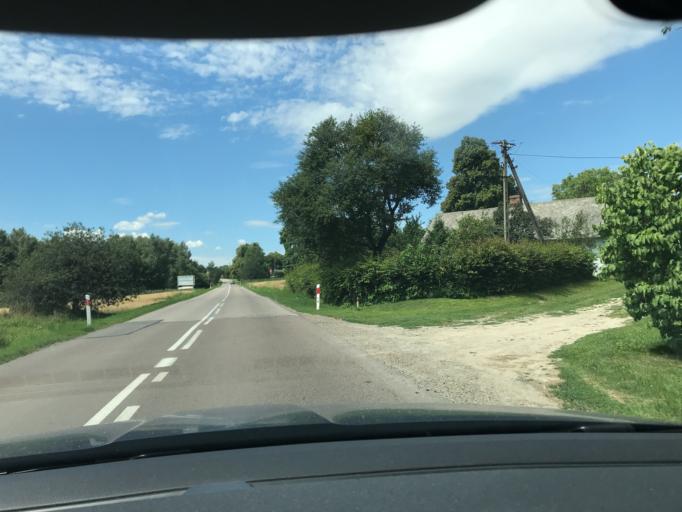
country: PL
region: Lublin Voivodeship
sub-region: Powiat zamojski
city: Szczebrzeszyn
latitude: 50.7137
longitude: 22.9175
